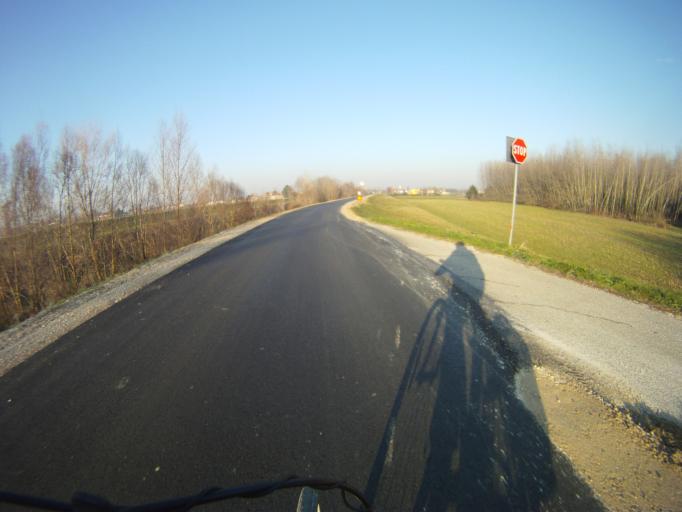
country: IT
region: Veneto
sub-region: Provincia di Padova
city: Legnaro
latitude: 45.3362
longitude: 11.9368
